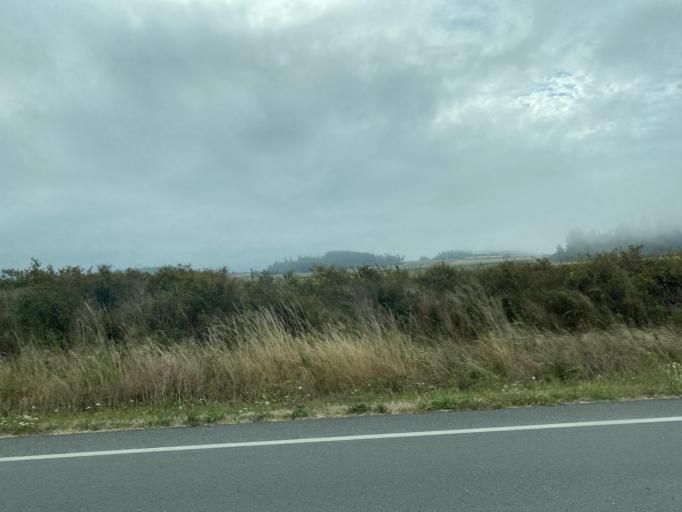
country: US
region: Washington
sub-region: Island County
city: Coupeville
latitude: 48.1969
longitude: -122.7017
